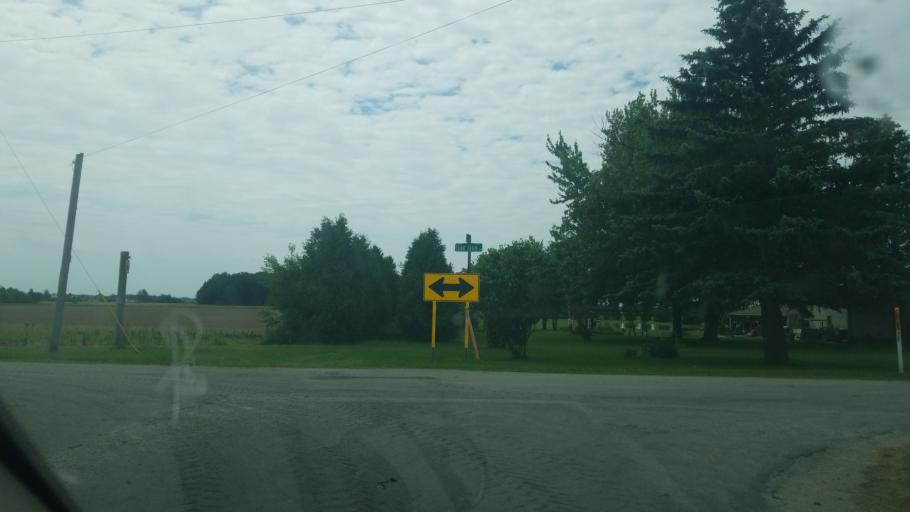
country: US
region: Ohio
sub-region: Wood County
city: North Baltimore
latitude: 41.2221
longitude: -83.6212
